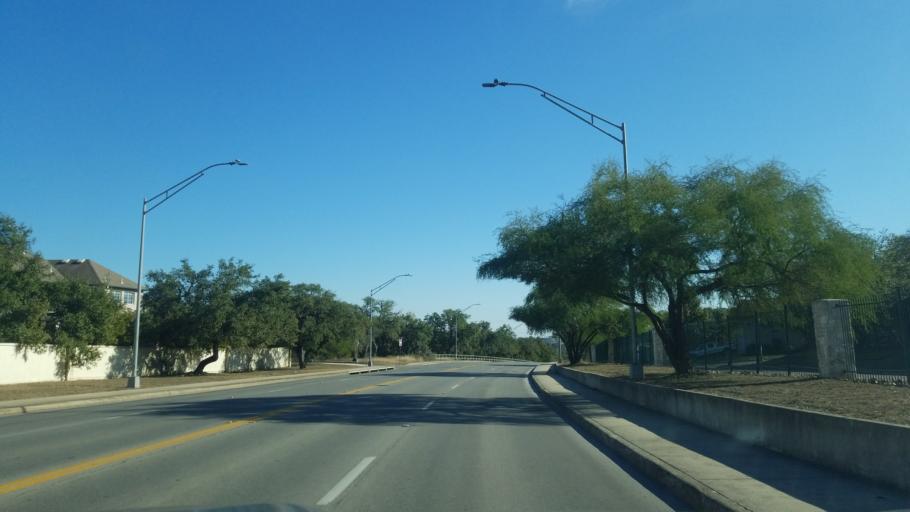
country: US
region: Texas
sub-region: Bexar County
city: Hollywood Park
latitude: 29.6346
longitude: -98.4829
